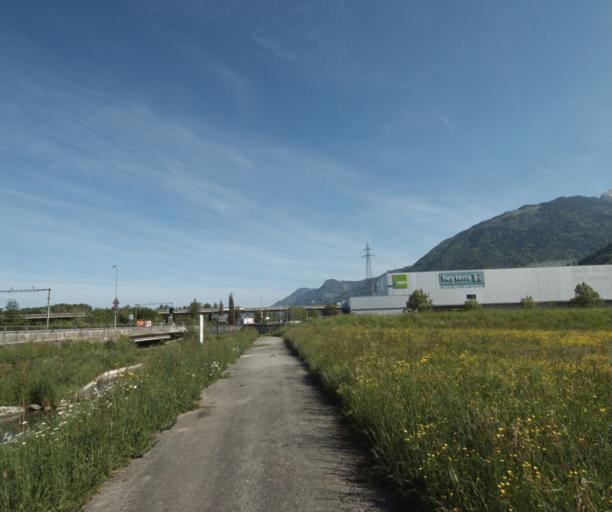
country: CH
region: Vaud
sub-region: Aigle District
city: Villeneuve
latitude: 46.3843
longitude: 6.9293
